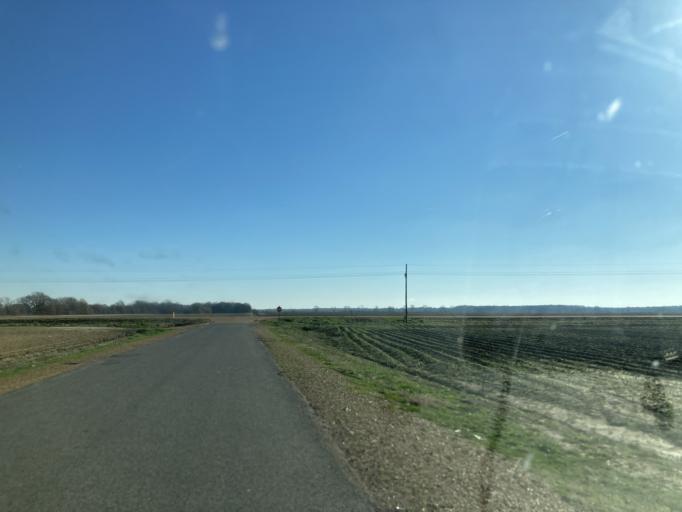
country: US
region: Mississippi
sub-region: Yazoo County
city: Yazoo City
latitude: 32.9519
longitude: -90.5858
